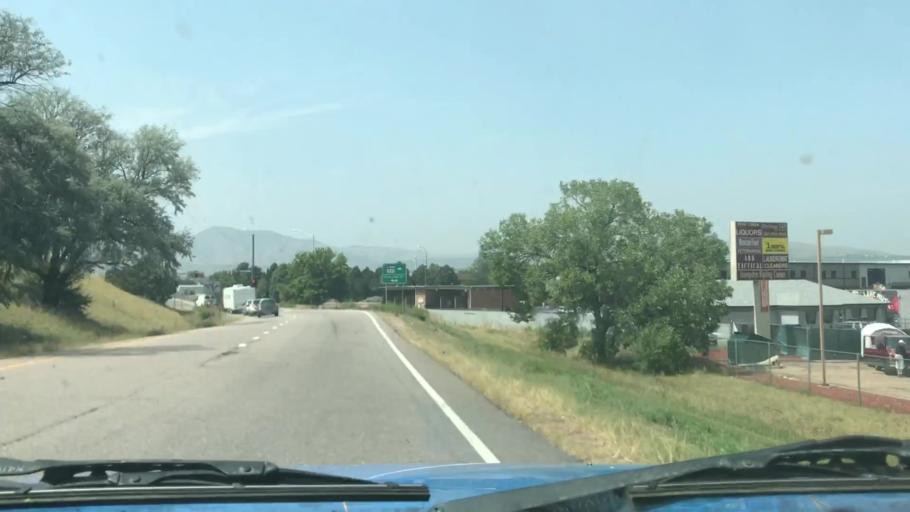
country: US
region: Colorado
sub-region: Jefferson County
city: Lakewood
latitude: 39.6540
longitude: -105.1078
